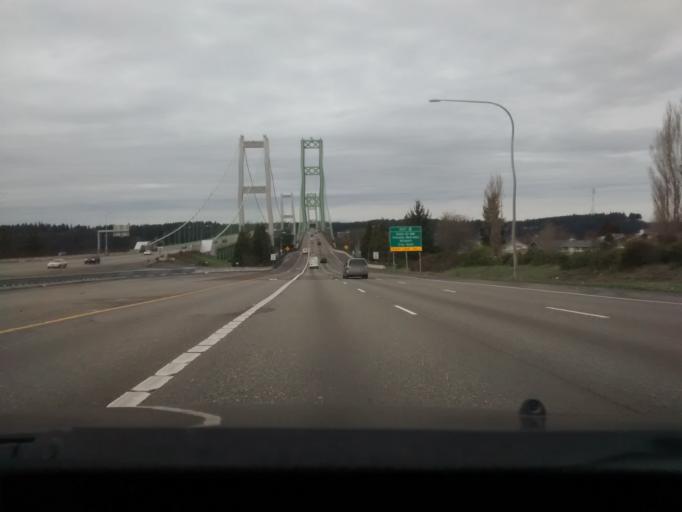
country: US
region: Washington
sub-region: Pierce County
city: University Place
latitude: 47.2609
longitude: -122.5411
